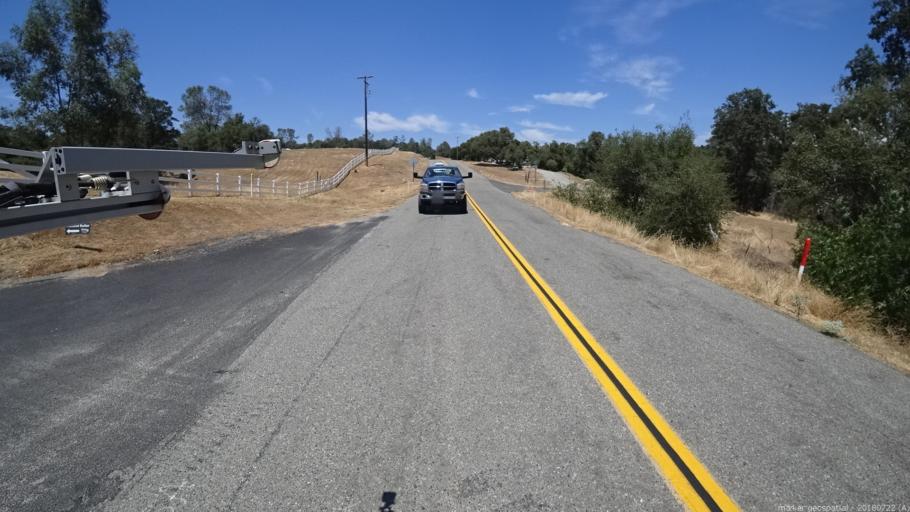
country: US
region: California
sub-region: Madera County
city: Yosemite Lakes
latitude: 37.2173
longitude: -119.7331
